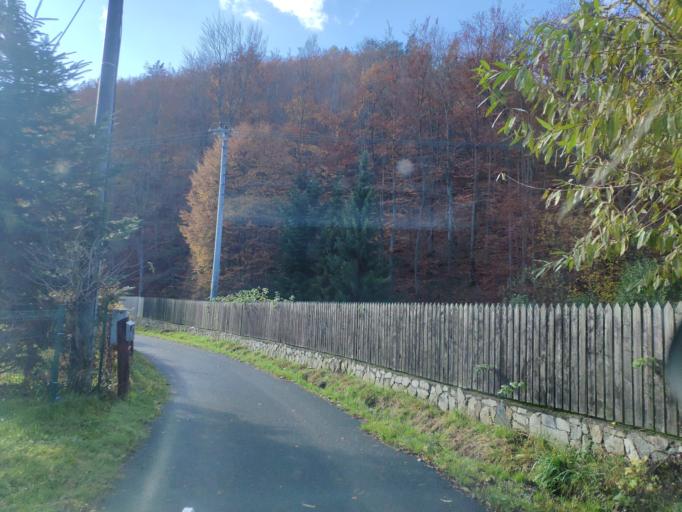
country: SK
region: Kosicky
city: Moldava nad Bodvou
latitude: 48.7431
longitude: 21.0171
